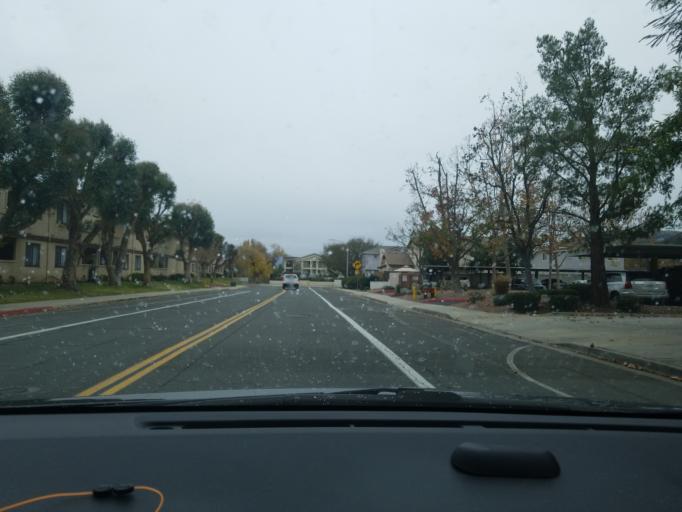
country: US
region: California
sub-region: Riverside County
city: Temecula
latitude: 33.4951
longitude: -117.1537
